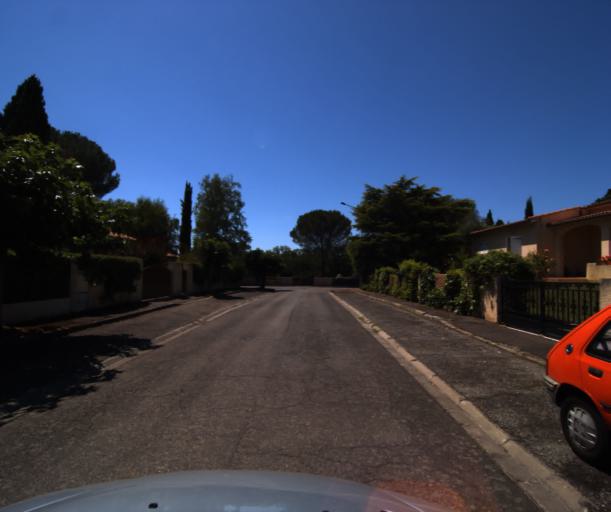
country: FR
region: Midi-Pyrenees
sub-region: Departement de la Haute-Garonne
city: Muret
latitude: 43.4506
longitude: 1.3268
